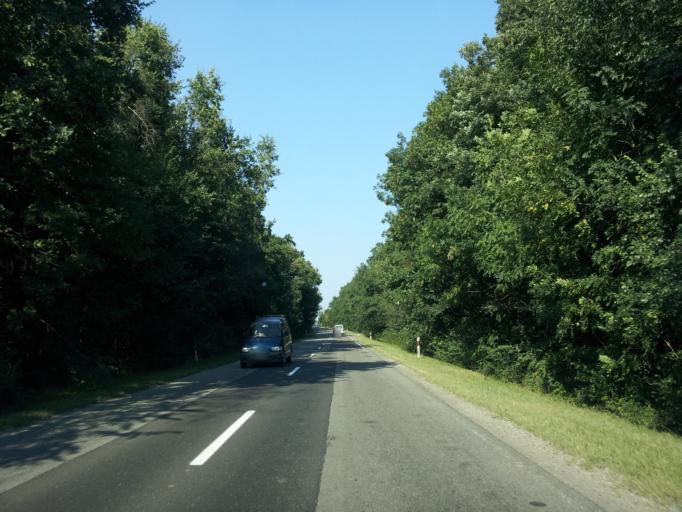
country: HU
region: Fejer
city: Polgardi
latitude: 47.0257
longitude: 18.2855
